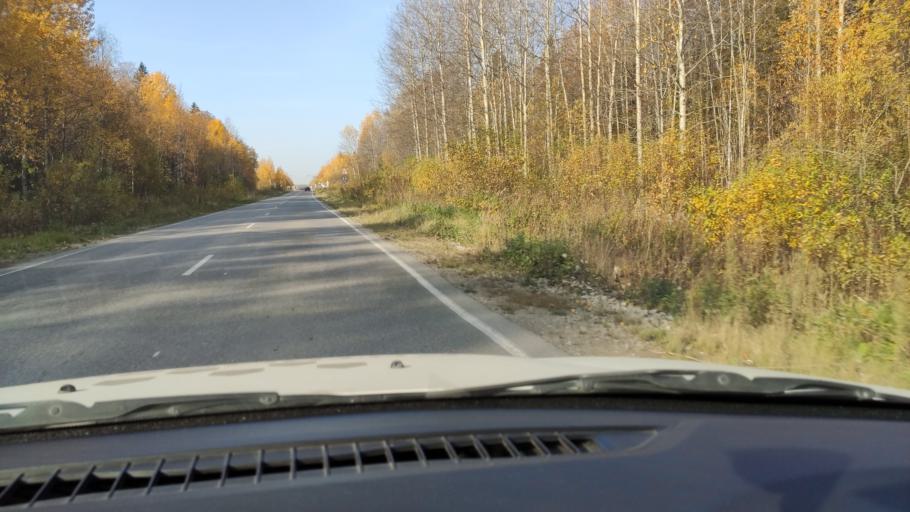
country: RU
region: Perm
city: Novyye Lyady
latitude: 58.0273
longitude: 56.6289
